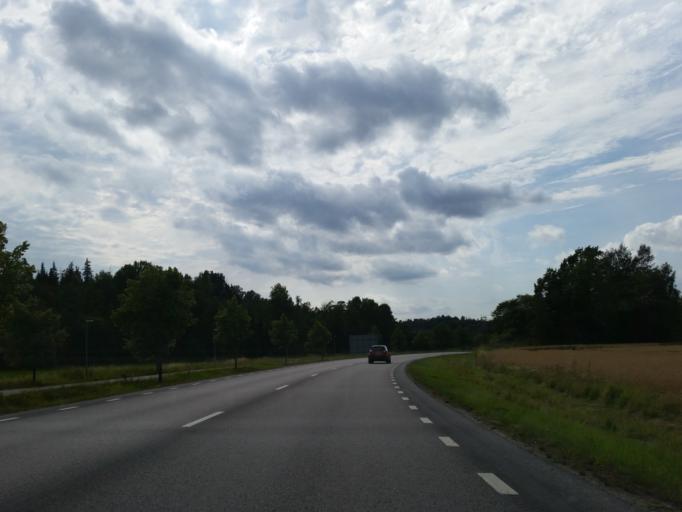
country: SE
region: Soedermanland
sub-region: Strangnas Kommun
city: Mariefred
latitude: 59.2517
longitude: 17.1745
